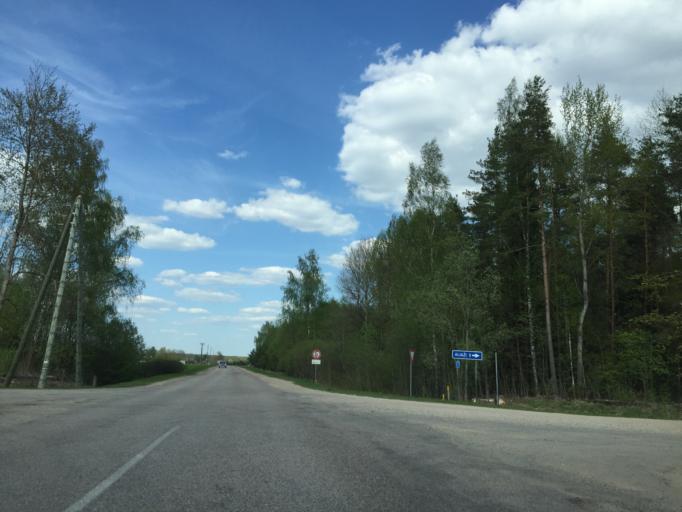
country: LV
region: Limbazu Rajons
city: Limbazi
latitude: 57.4224
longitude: 24.7056
